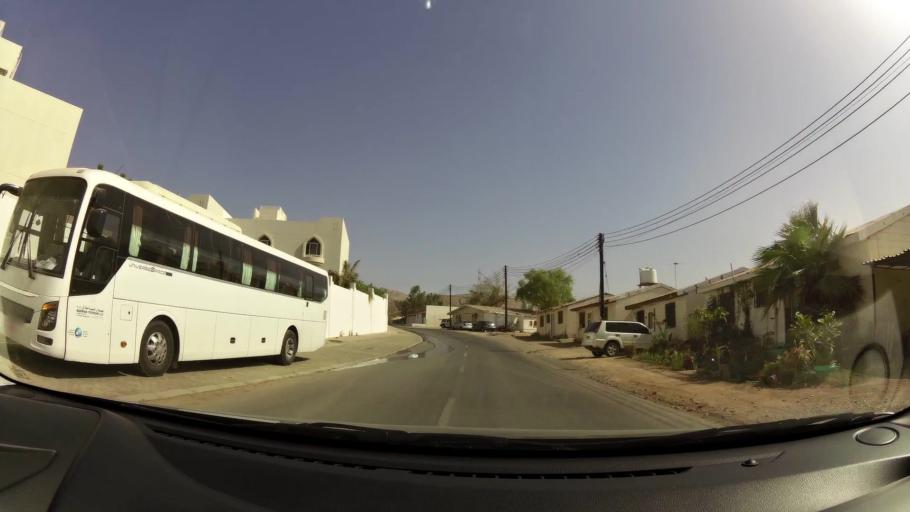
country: OM
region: Muhafazat Masqat
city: Muscat
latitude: 23.6040
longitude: 58.4948
